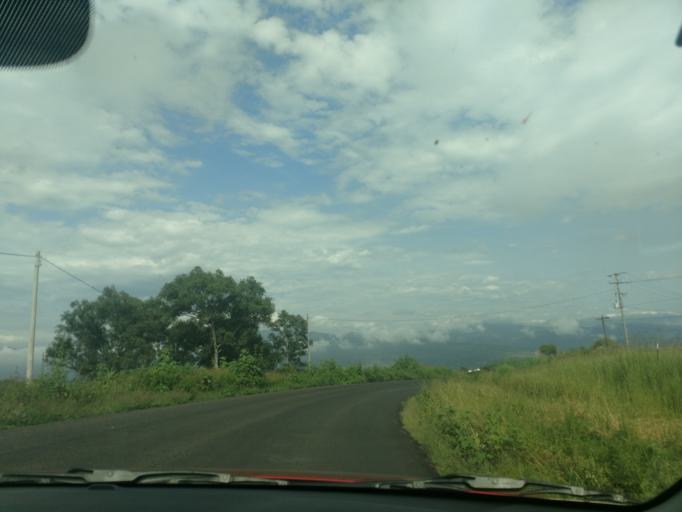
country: MX
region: Jalisco
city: El Salto
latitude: 20.4332
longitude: -104.4519
